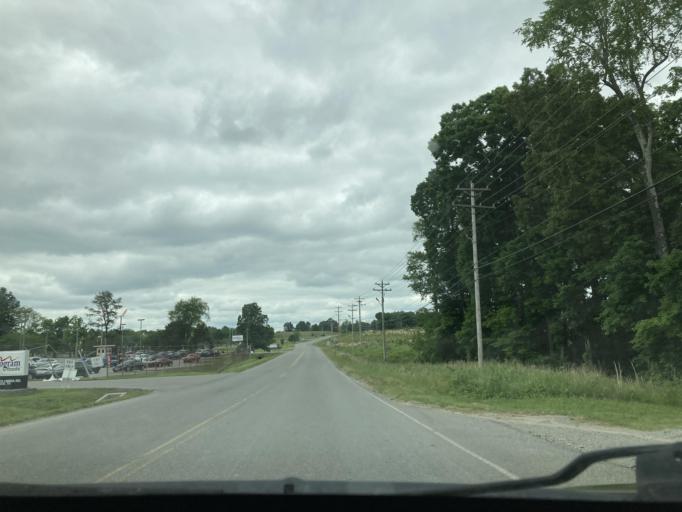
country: US
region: Tennessee
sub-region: Dickson County
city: Burns
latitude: 36.0462
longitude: -87.3433
